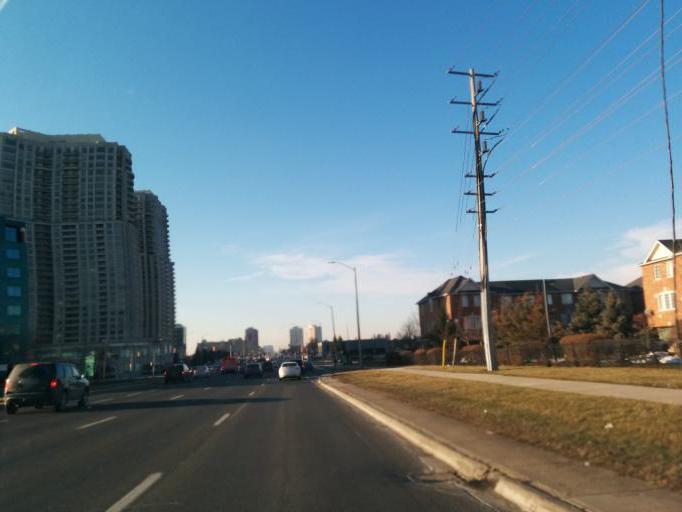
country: CA
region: Ontario
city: Mississauga
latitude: 43.6031
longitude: -79.6475
